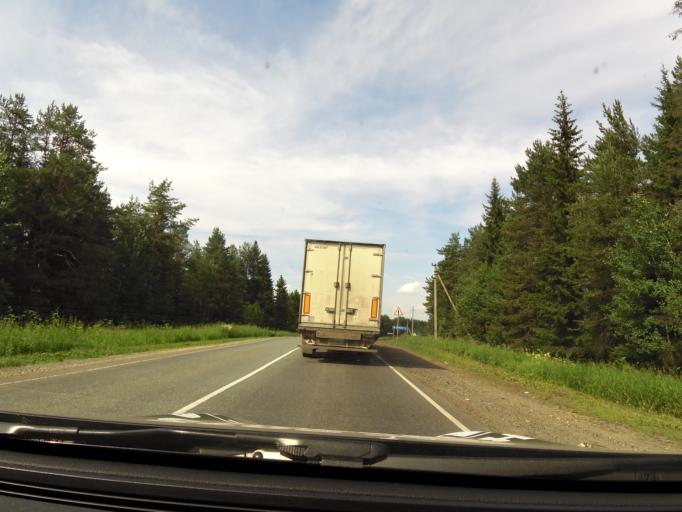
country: RU
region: Kirov
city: Slobodskoy
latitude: 58.7531
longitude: 50.3233
